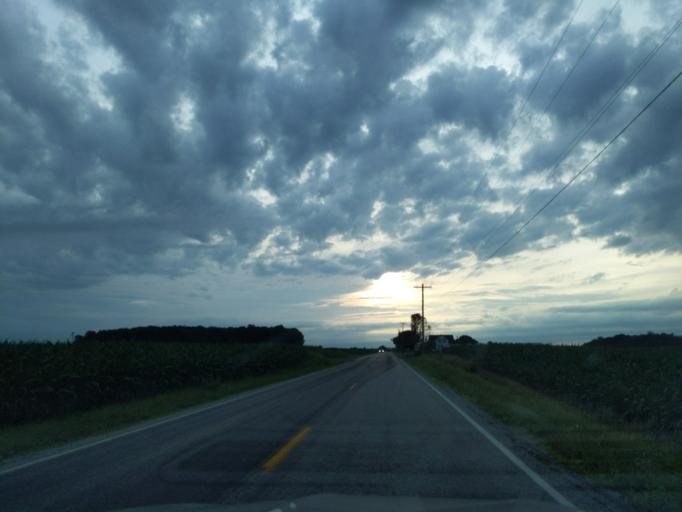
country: US
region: Indiana
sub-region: Ripley County
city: Osgood
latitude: 39.1997
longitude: -85.3051
